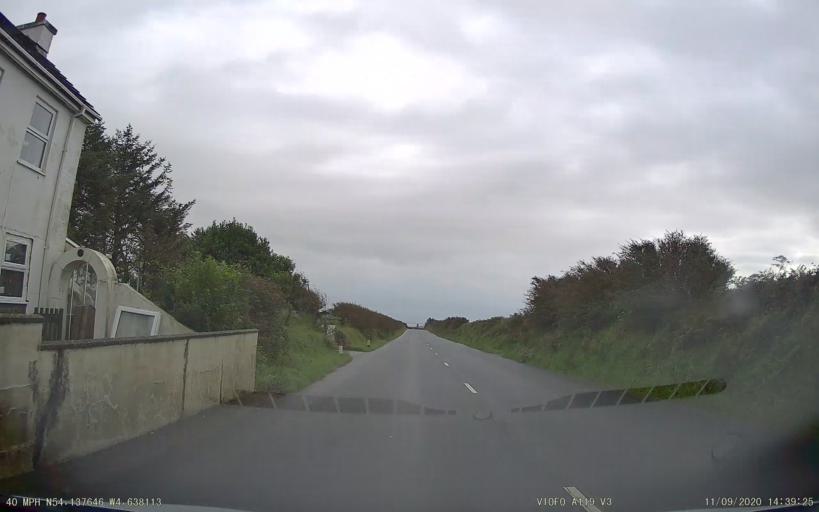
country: IM
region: Castletown
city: Castletown
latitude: 54.1376
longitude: -4.6381
